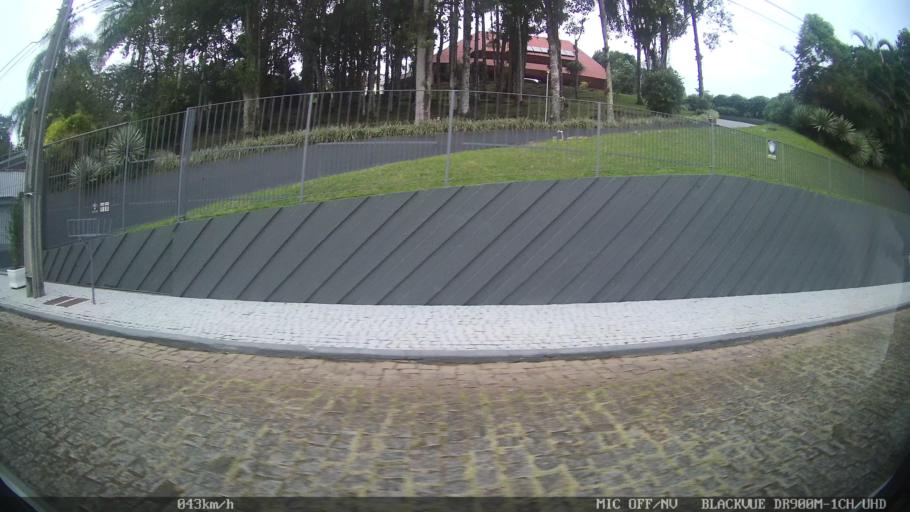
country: BR
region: Santa Catarina
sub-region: Joinville
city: Joinville
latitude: -26.2961
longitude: -48.8565
